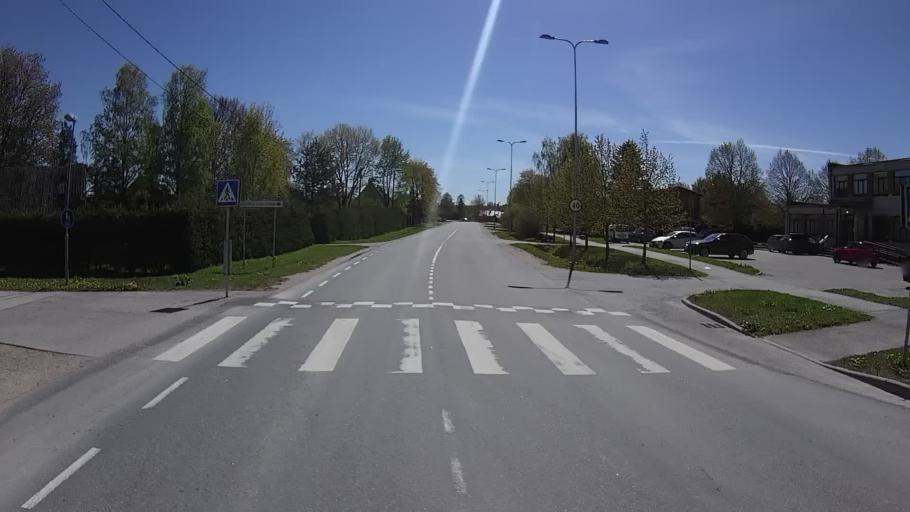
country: EE
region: Harju
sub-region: Raasiku vald
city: Raasiku
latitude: 59.1836
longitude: 25.1676
